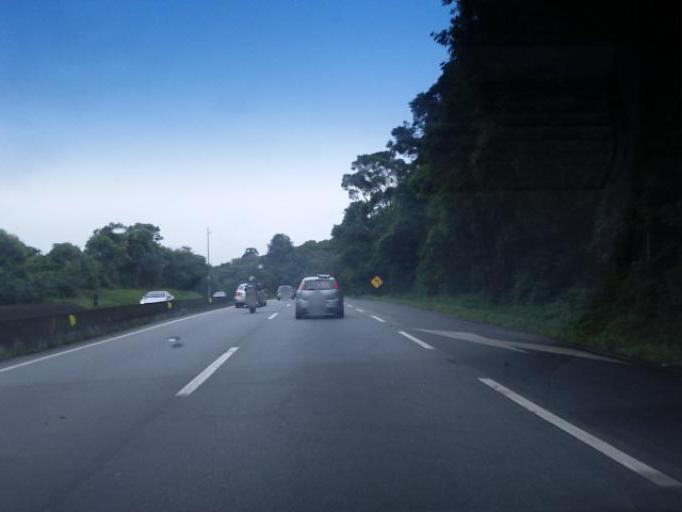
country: BR
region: Parana
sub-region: Sao Jose Dos Pinhais
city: Sao Jose dos Pinhais
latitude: -25.8451
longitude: -49.0789
